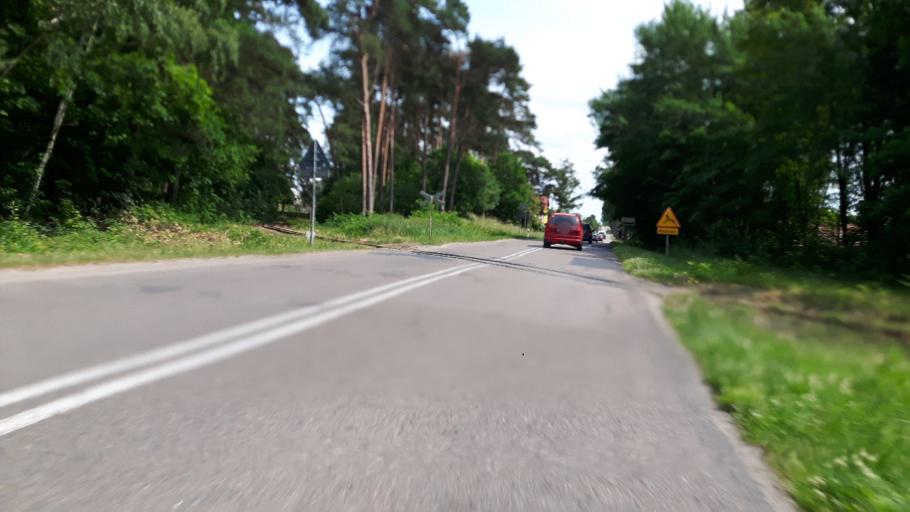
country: PL
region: Pomeranian Voivodeship
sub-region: Powiat nowodworski
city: Stegna
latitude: 54.3307
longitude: 19.0986
